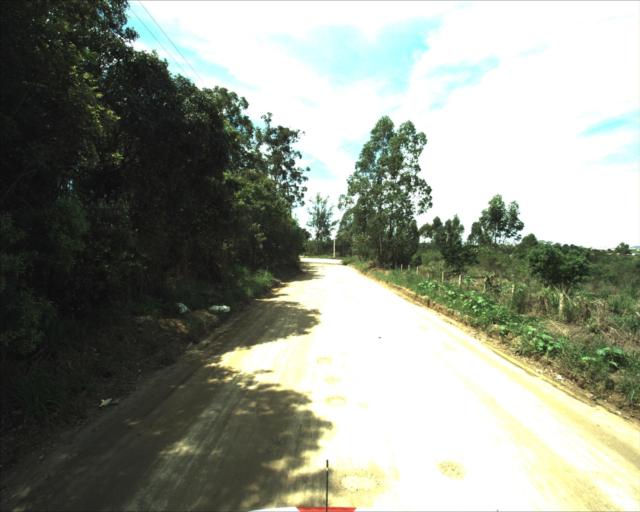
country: BR
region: Sao Paulo
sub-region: Aracoiaba Da Serra
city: Aracoiaba da Serra
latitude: -23.5548
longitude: -47.5415
